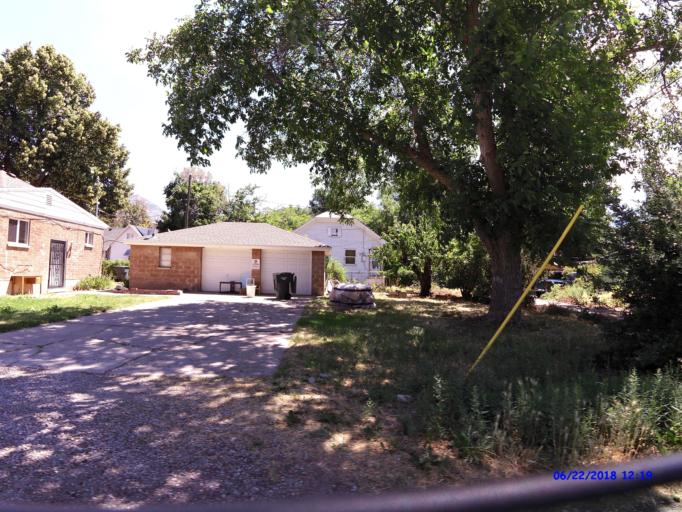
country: US
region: Utah
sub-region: Weber County
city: Ogden
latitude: 41.2372
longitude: -111.9678
